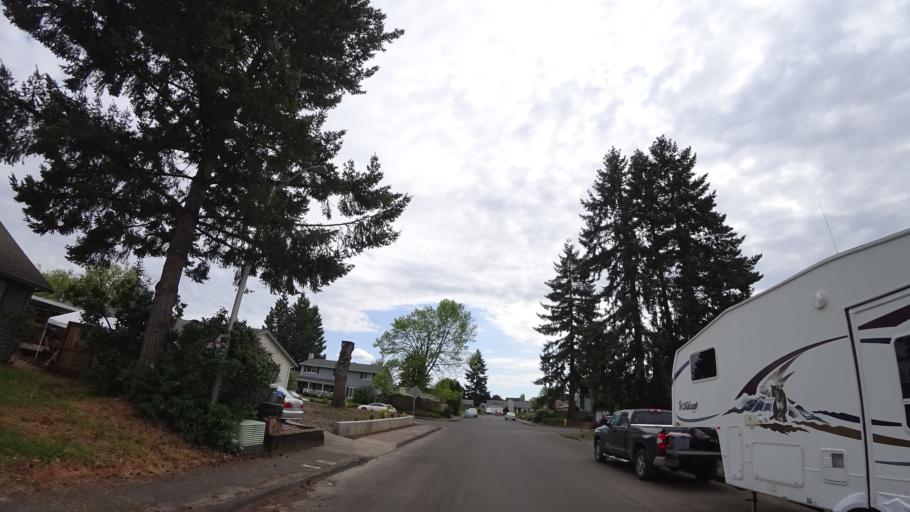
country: US
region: Oregon
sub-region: Washington County
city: Hillsboro
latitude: 45.4978
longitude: -122.9648
